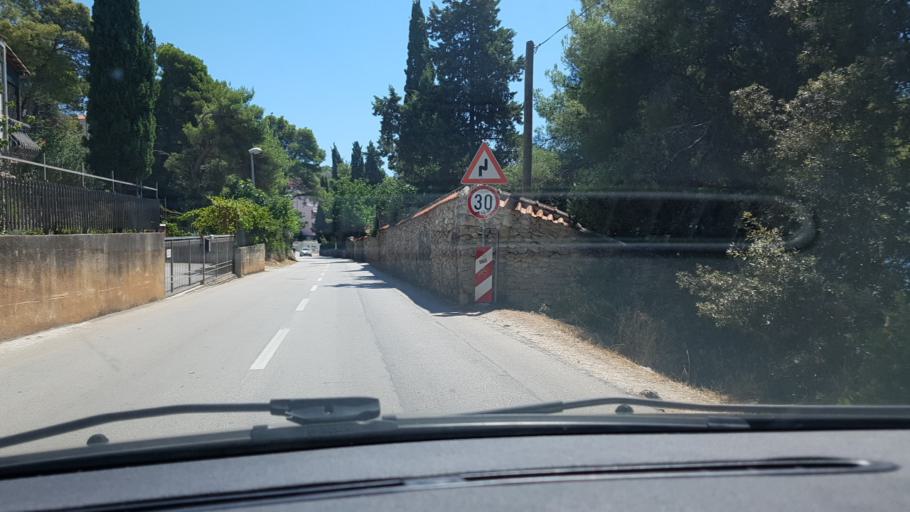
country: HR
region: Splitsko-Dalmatinska
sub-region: Grad Trogir
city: Trogir
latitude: 43.5112
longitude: 16.2528
